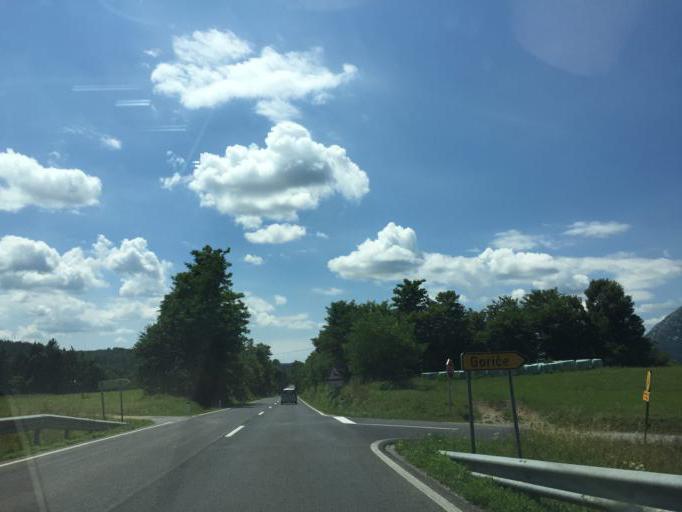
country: SI
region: Postojna
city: Postojna
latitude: 45.7699
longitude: 14.1356
